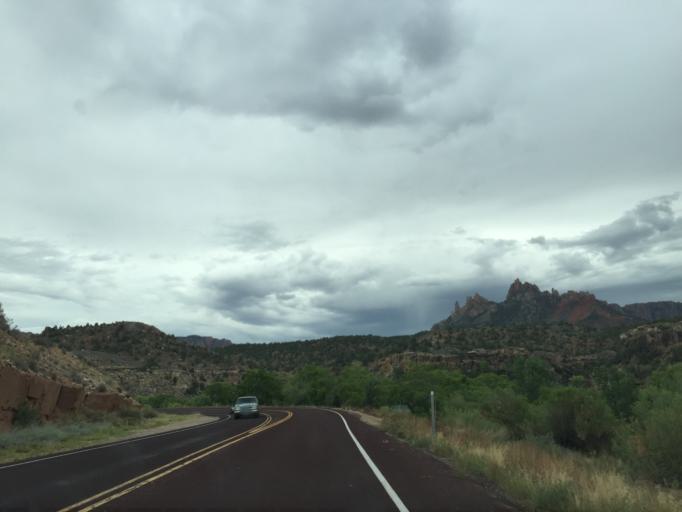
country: US
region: Utah
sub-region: Washington County
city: Hildale
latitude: 37.1618
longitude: -113.0222
